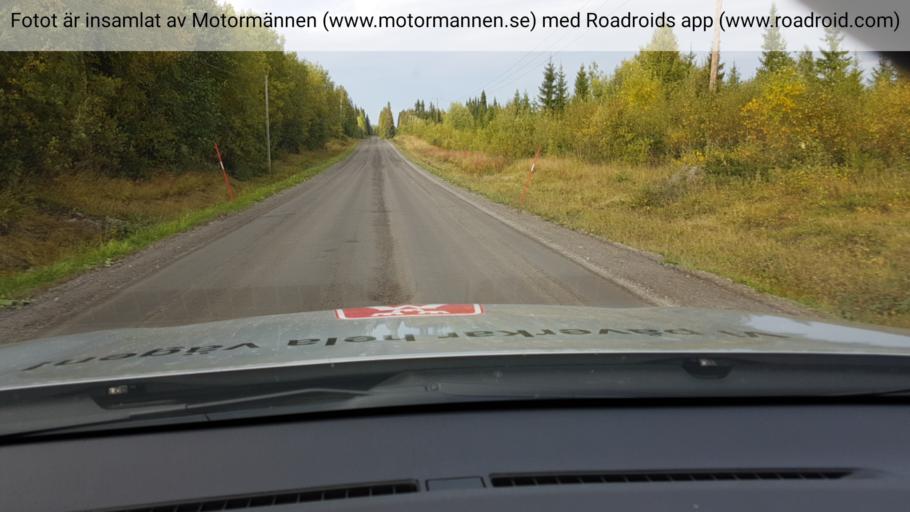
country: SE
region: Jaemtland
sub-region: Stroemsunds Kommun
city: Stroemsund
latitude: 63.9947
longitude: 15.8166
